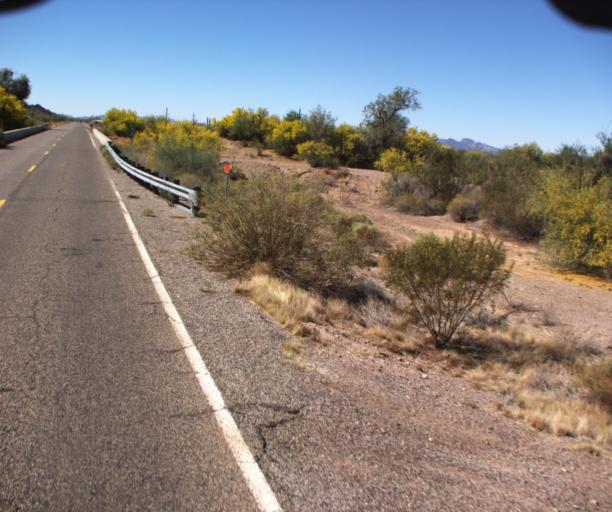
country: US
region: Arizona
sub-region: Pima County
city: Ajo
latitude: 32.2404
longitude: -112.7497
